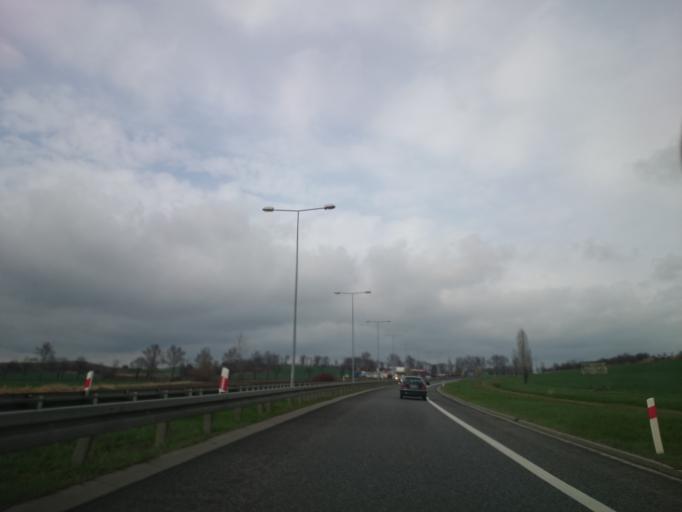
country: PL
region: Opole Voivodeship
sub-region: Powiat nyski
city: Otmuchow
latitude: 50.4636
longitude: 17.1979
